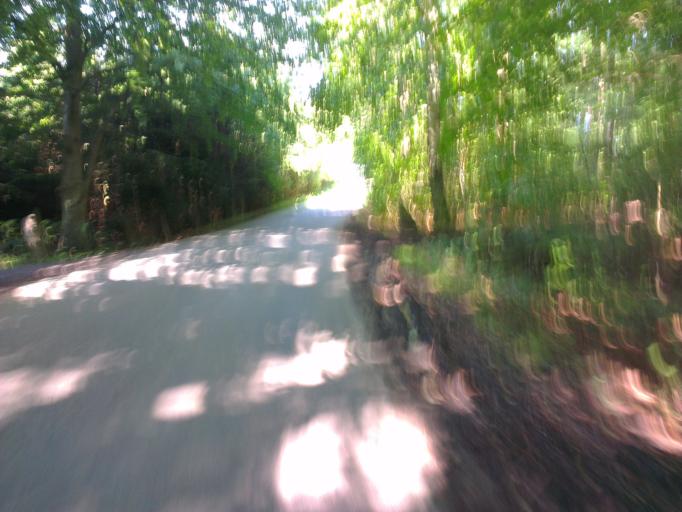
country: DK
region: Capital Region
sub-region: Frederikssund Kommune
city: Skibby
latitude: 55.7194
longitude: 11.9512
